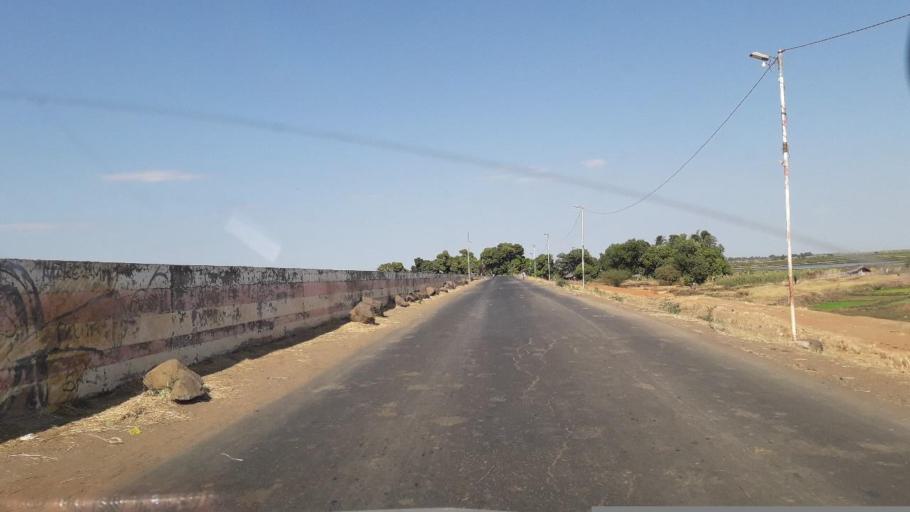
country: MG
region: Boeny
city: Marovoay
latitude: -16.1188
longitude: 46.7498
